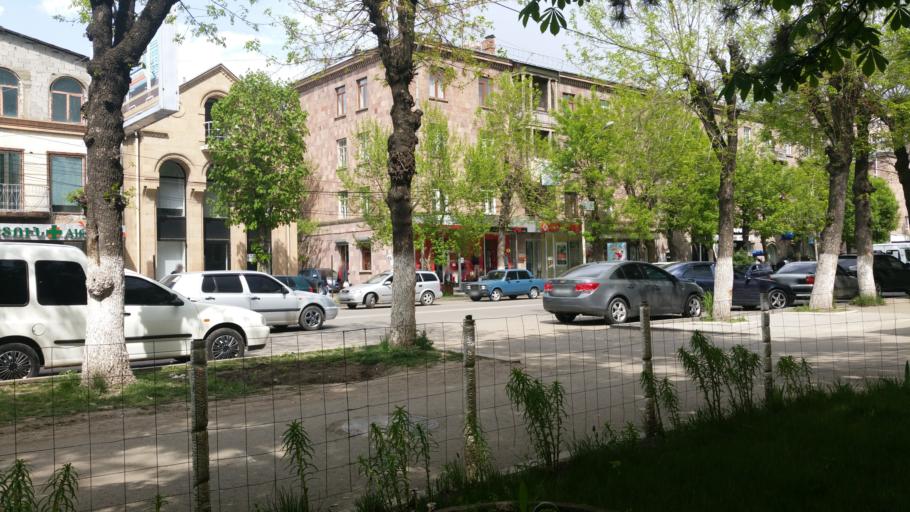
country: AM
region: Lorri
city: Vanadzor
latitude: 40.8106
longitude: 44.4868
